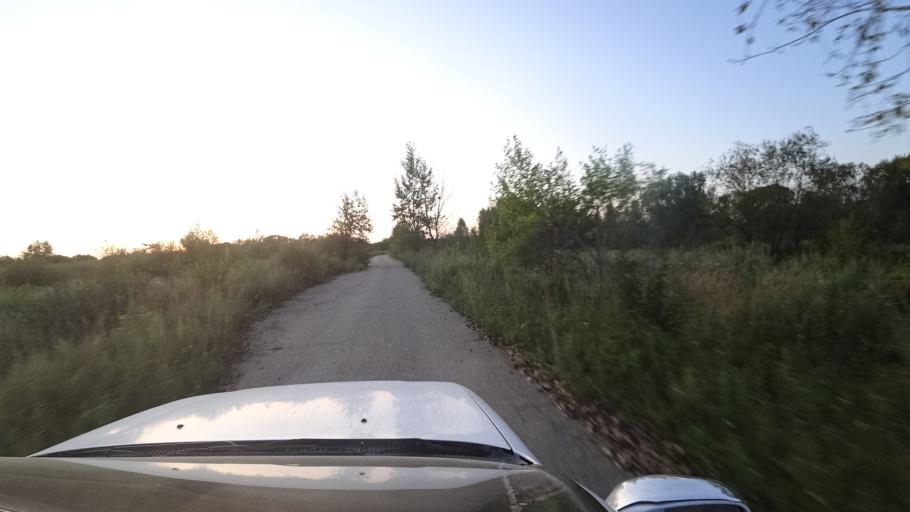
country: RU
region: Primorskiy
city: Dal'nerechensk
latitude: 45.9489
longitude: 133.7619
